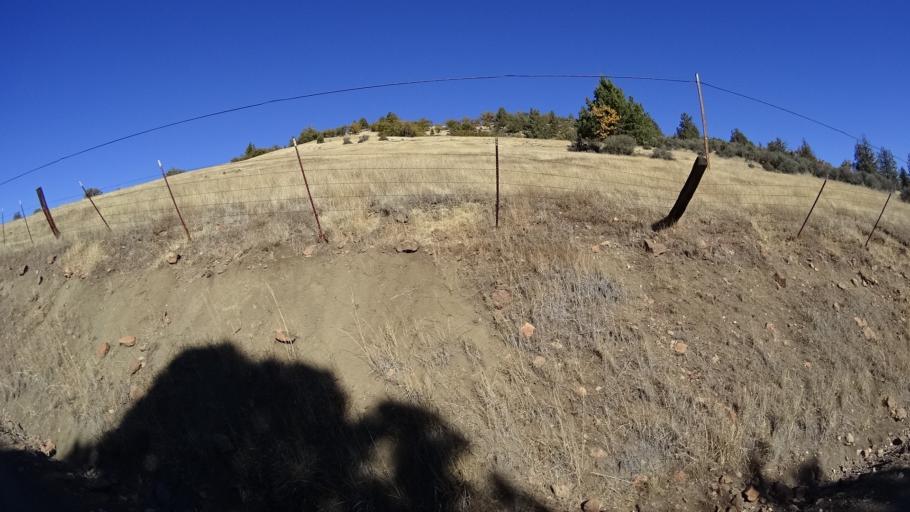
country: US
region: California
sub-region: Siskiyou County
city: Montague
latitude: 41.9618
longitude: -122.3129
